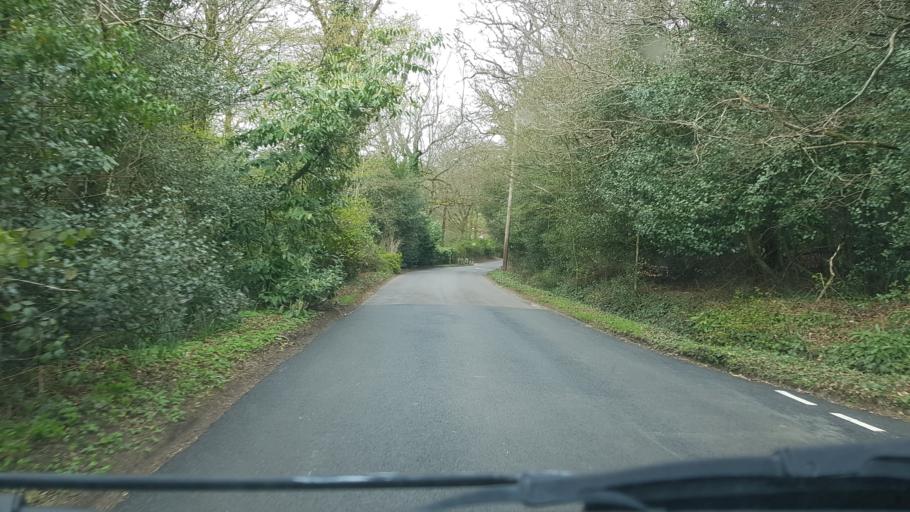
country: GB
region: England
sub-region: Surrey
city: Cranleigh
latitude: 51.1680
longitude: -0.4537
